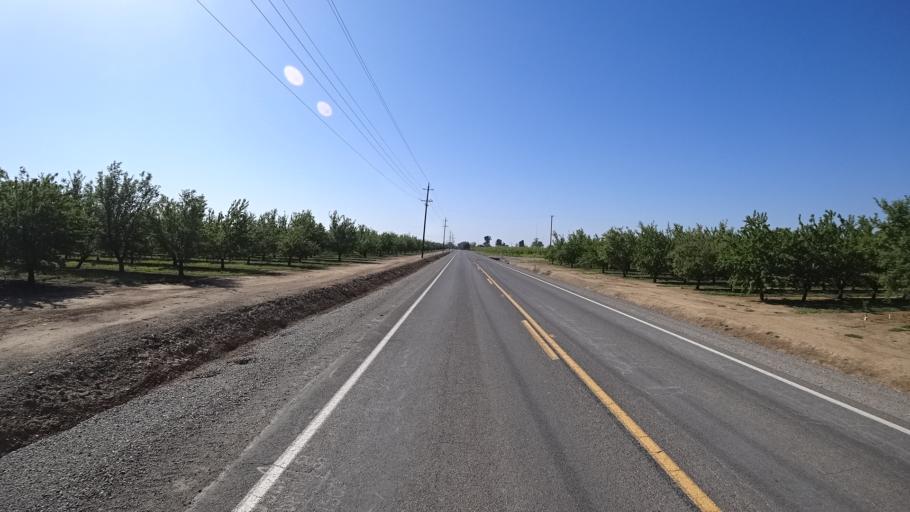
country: US
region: California
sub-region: Glenn County
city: Hamilton City
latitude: 39.6387
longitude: -122.0074
